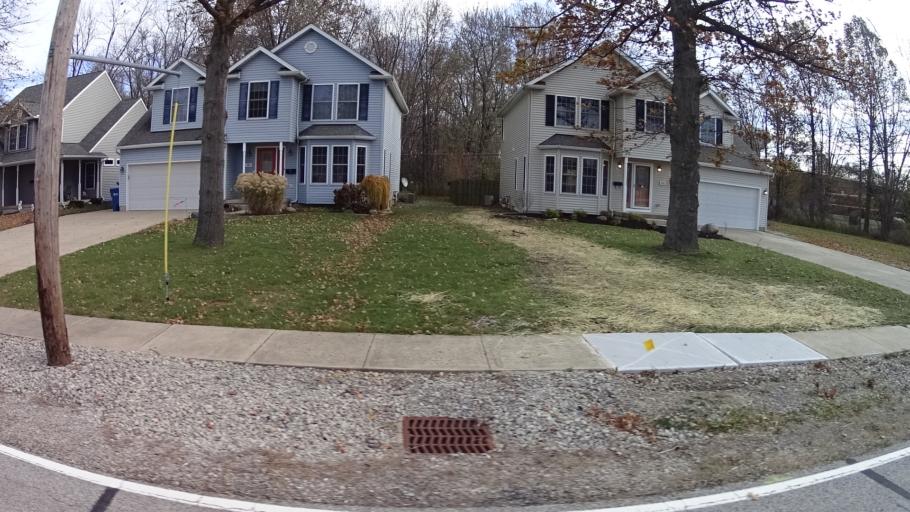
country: US
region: Ohio
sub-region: Lorain County
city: Avon Lake
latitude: 41.4969
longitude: -82.0616
